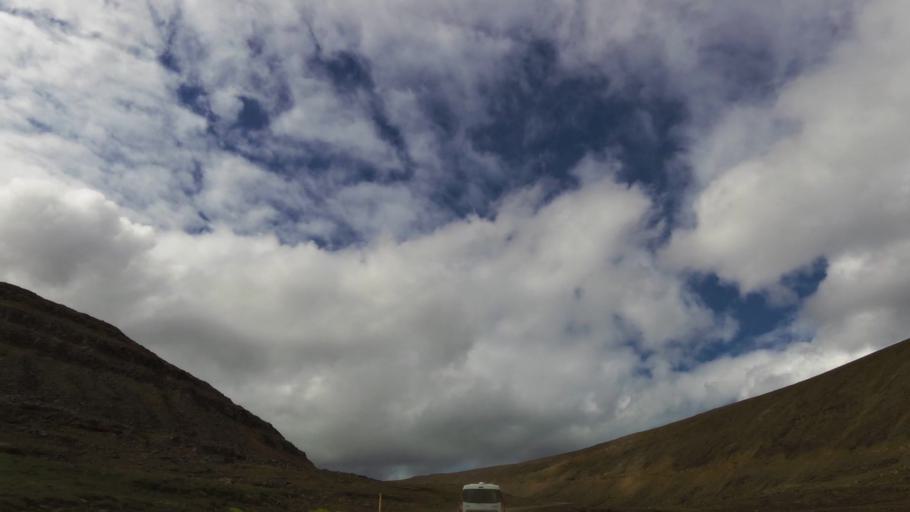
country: IS
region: Westfjords
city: Isafjoerdur
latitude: 66.1705
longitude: -23.3513
